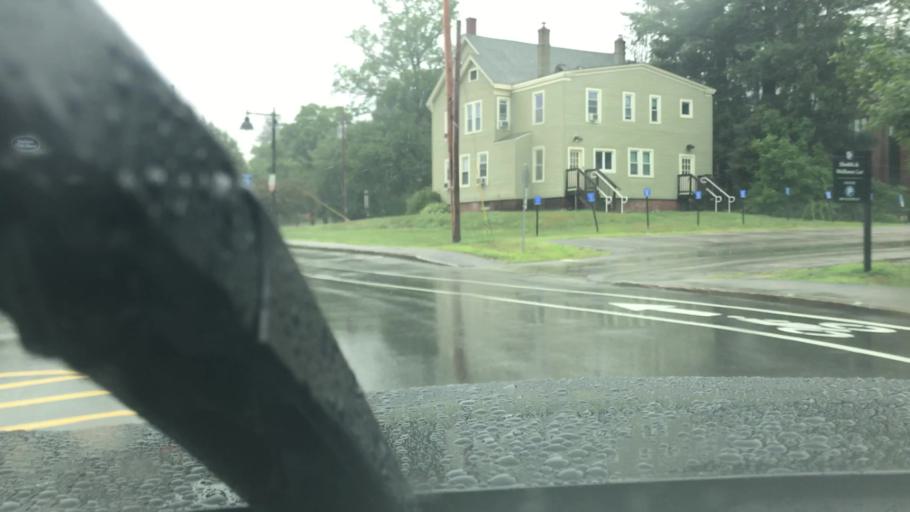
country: US
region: New Hampshire
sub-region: Strafford County
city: Durham
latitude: 43.1358
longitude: -70.9278
